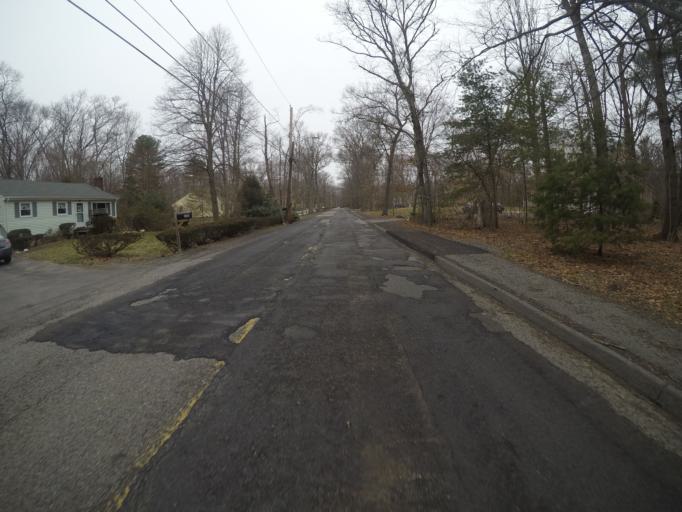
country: US
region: Massachusetts
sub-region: Bristol County
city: Easton
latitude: 42.0537
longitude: -71.1419
